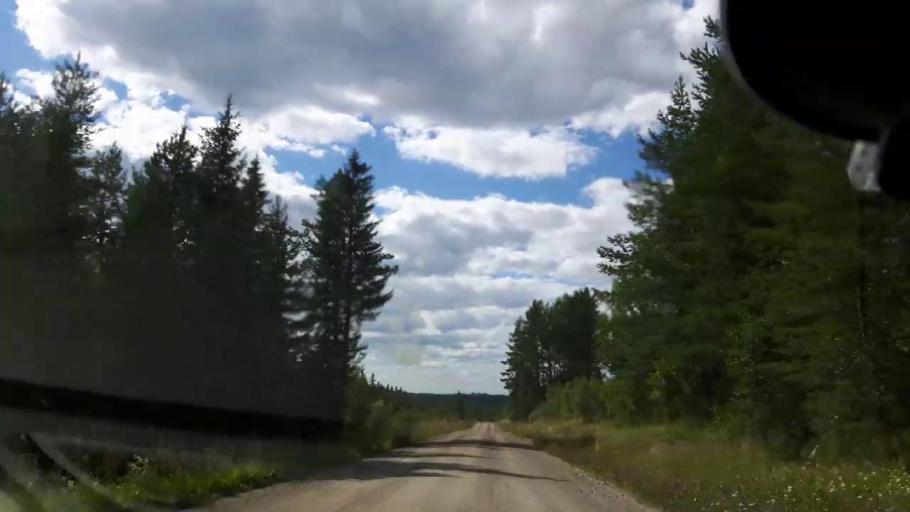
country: SE
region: Jaemtland
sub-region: Braecke Kommun
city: Braecke
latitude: 62.7214
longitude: 15.5546
